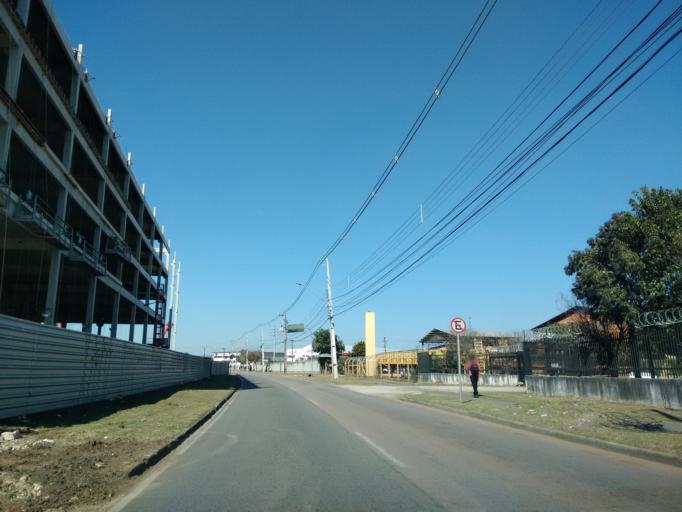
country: BR
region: Parana
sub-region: Curitiba
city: Curitiba
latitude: -25.5178
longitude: -49.3252
